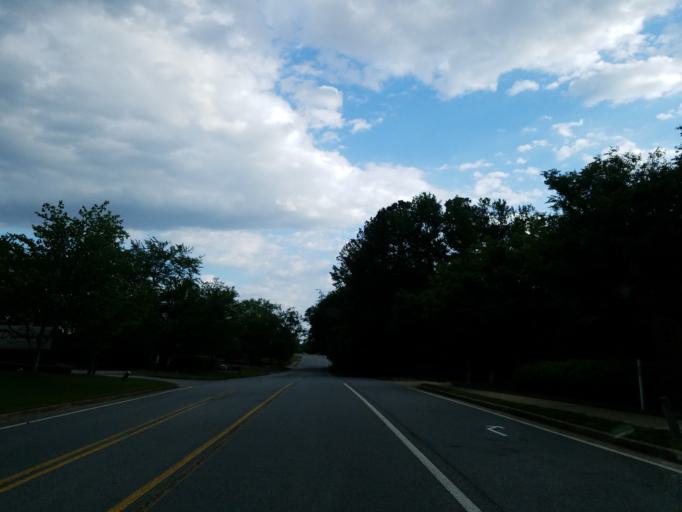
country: US
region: Georgia
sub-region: Fulton County
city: Roswell
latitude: 34.0418
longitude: -84.3437
